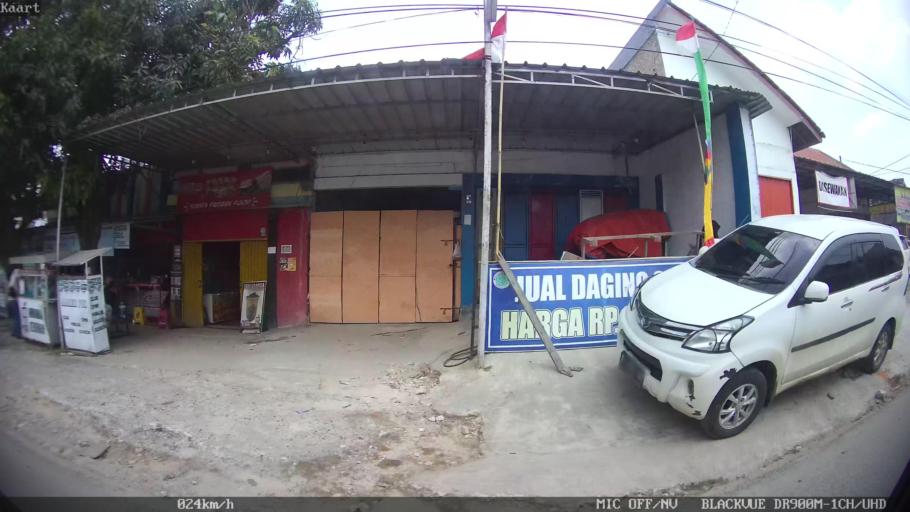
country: ID
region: Lampung
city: Pringsewu
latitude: -5.3480
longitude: 104.9757
